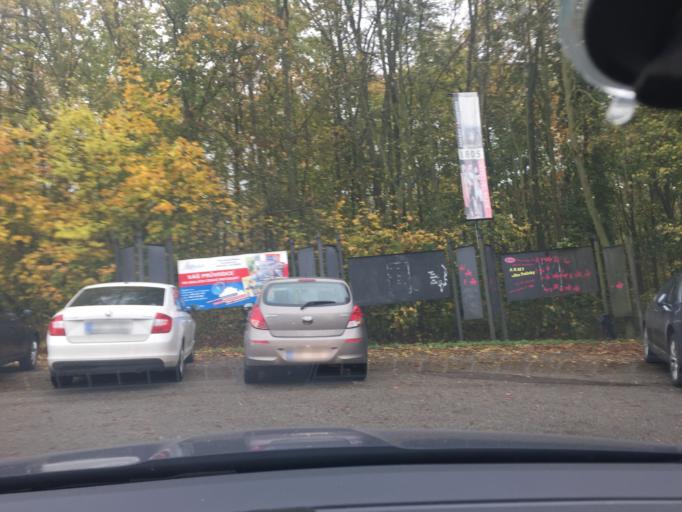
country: CZ
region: South Moravian
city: Sokolnice
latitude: 49.1272
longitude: 16.7620
